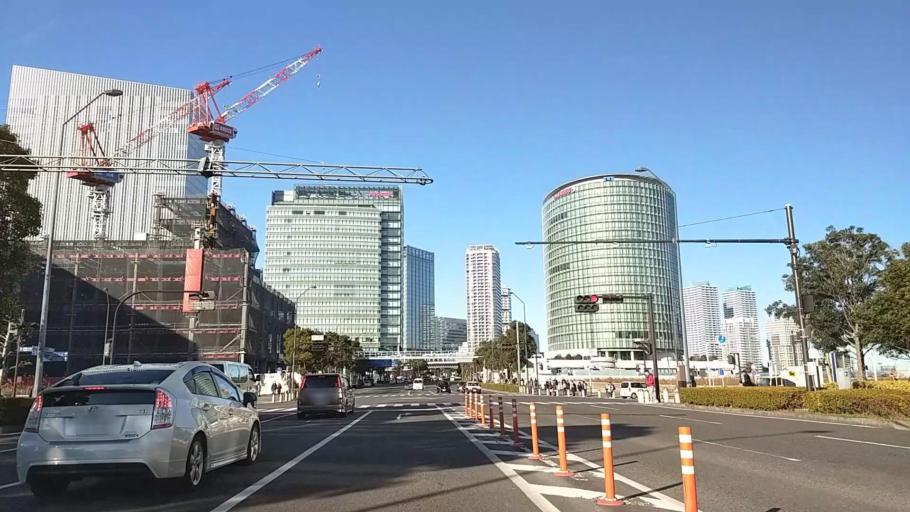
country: JP
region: Kanagawa
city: Yokohama
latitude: 35.4602
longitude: 139.6266
